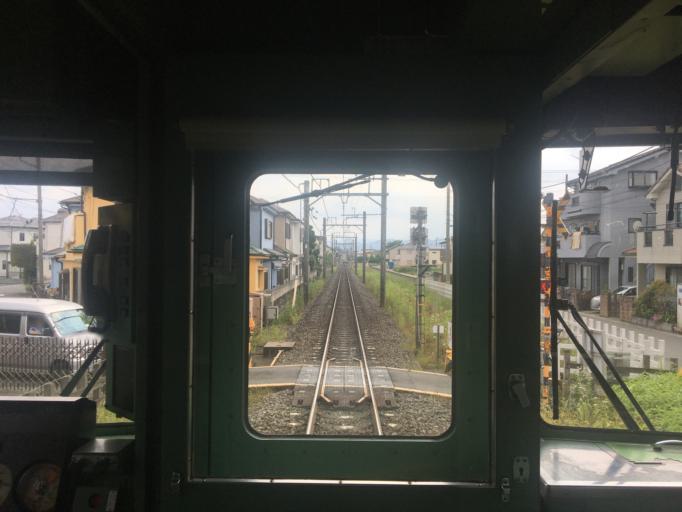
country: JP
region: Saitama
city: Sakado
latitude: 35.9439
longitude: 139.3751
